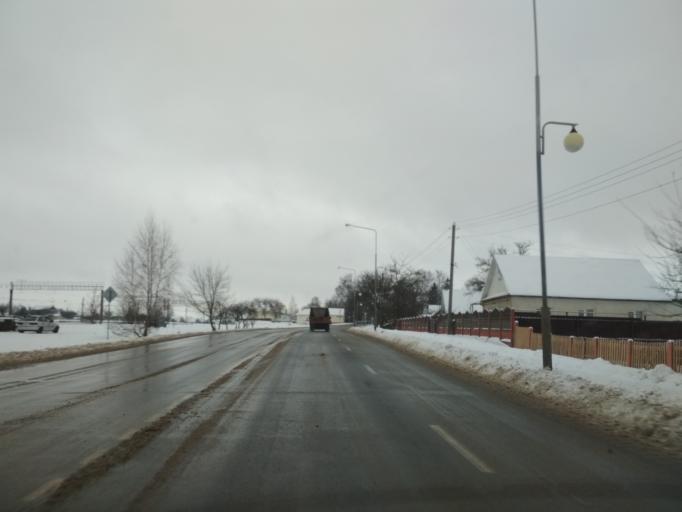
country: BY
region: Minsk
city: Mar''ina Horka
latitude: 53.5039
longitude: 28.1476
